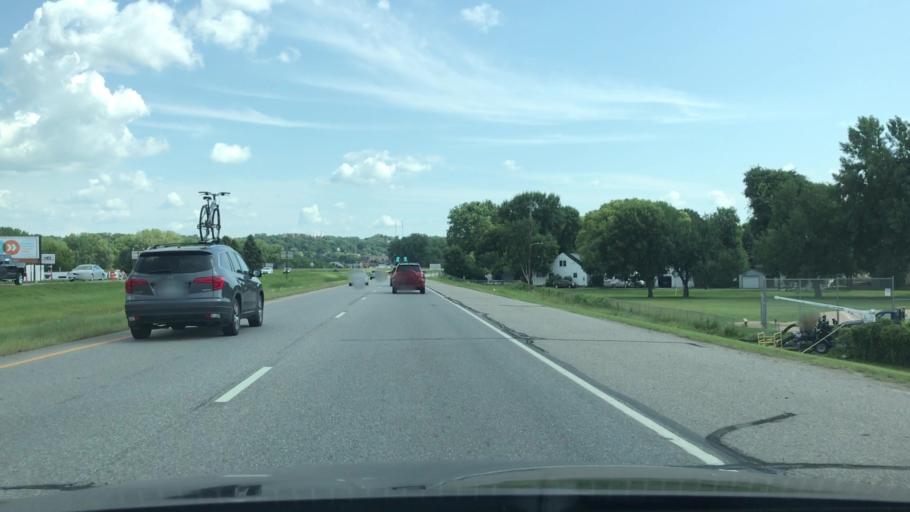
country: US
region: Minnesota
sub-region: Blue Earth County
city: Mankato
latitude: 44.1805
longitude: -94.0071
